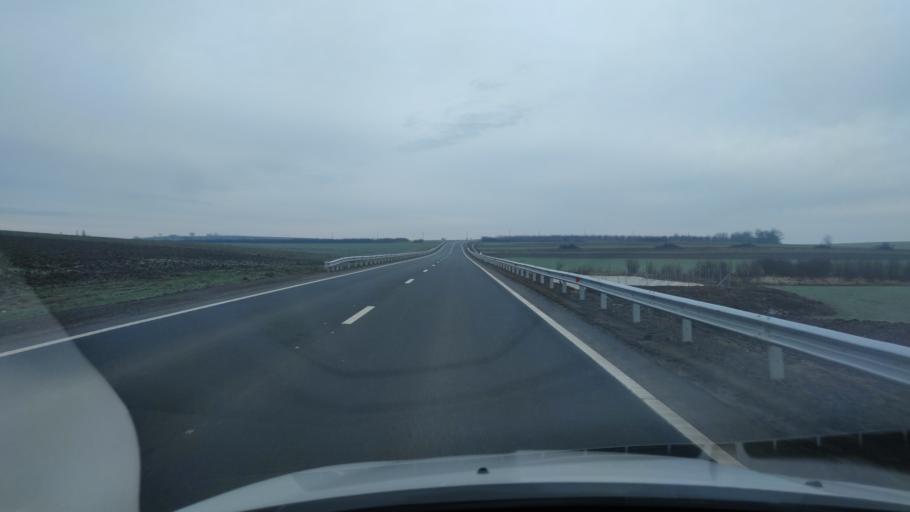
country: RO
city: Szekelyhid
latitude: 47.3315
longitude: 22.0935
